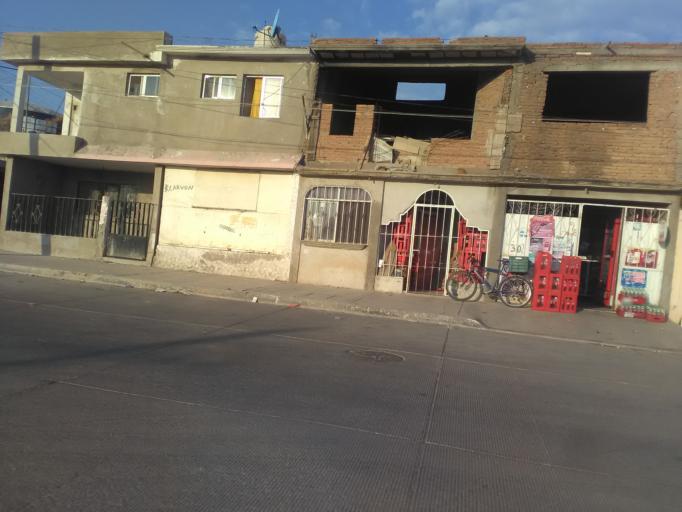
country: MX
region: Durango
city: Victoria de Durango
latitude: 24.0486
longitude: -104.6483
